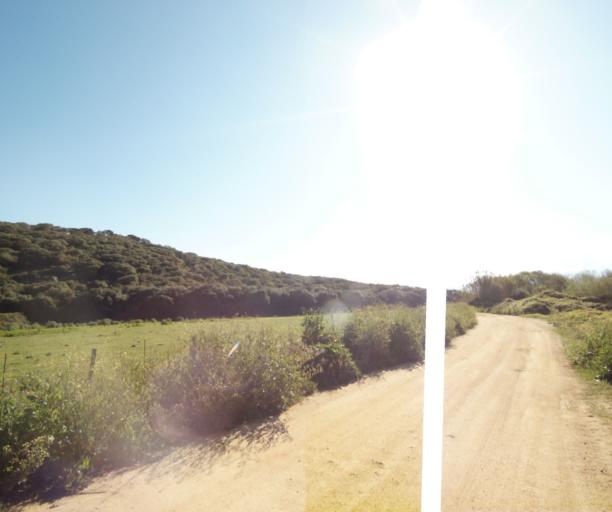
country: FR
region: Corsica
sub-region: Departement de la Corse-du-Sud
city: Propriano
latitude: 41.6635
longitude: 8.8941
